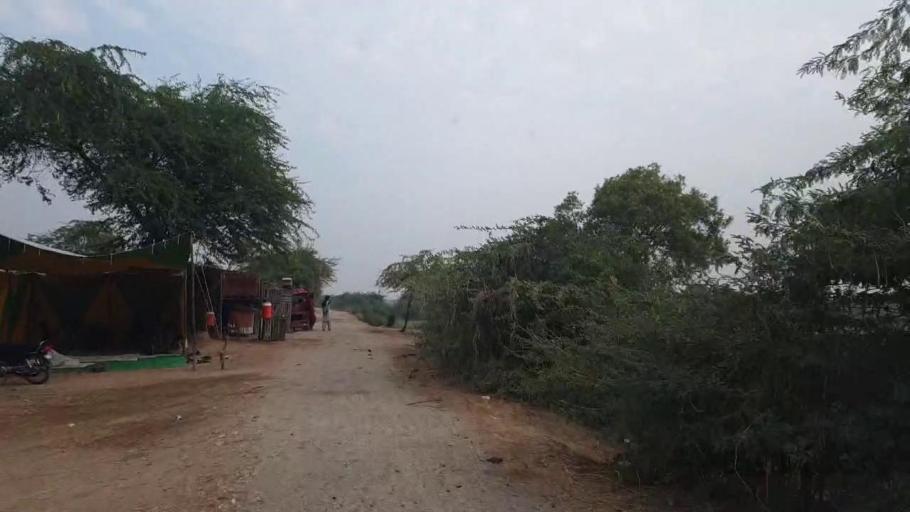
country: PK
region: Sindh
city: Talhar
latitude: 24.8265
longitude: 68.8795
